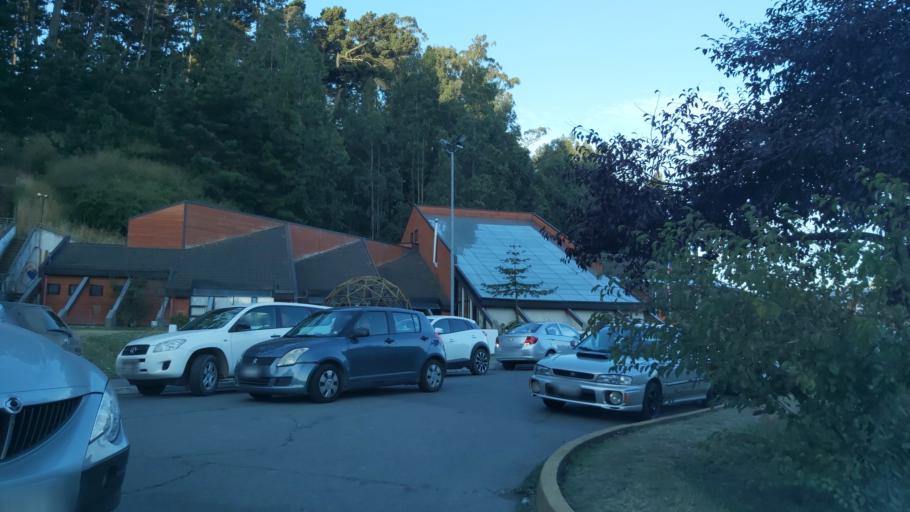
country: CL
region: Biobio
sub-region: Provincia de Concepcion
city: Concepcion
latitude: -36.8454
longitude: -73.1075
